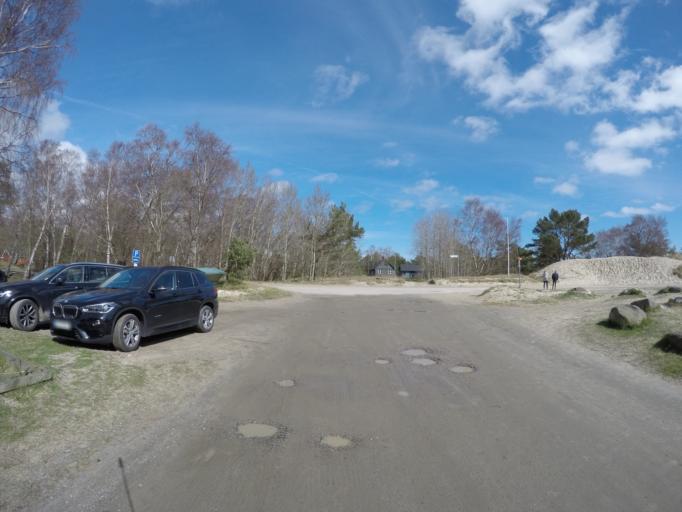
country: SE
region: Skane
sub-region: Simrishamns Kommun
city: Simrishamn
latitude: 55.3861
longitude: 14.1958
